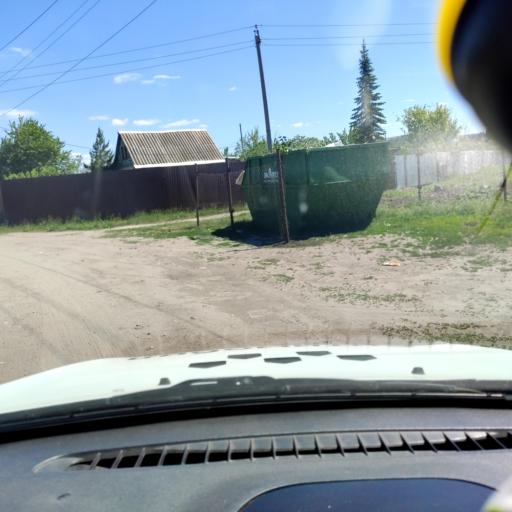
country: RU
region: Samara
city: Tol'yatti
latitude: 53.6089
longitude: 49.4556
